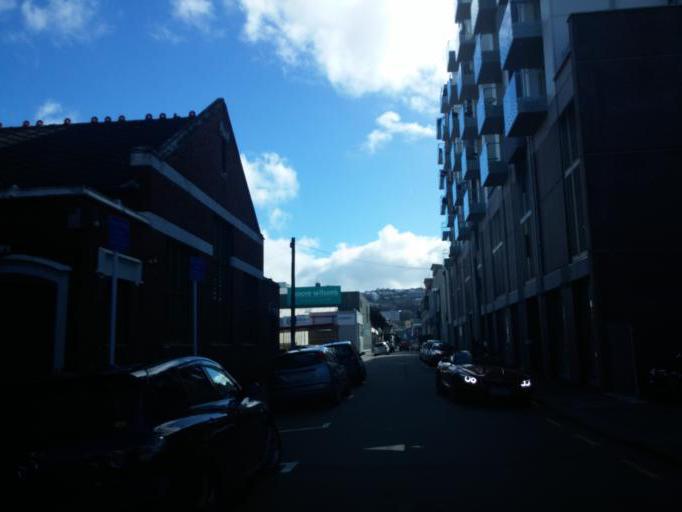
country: NZ
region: Wellington
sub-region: Wellington City
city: Wellington
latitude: -41.2958
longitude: 174.7824
